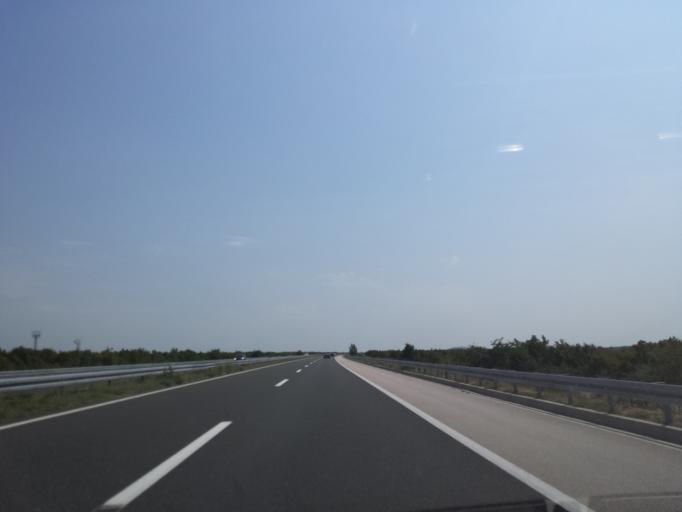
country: HR
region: Zadarska
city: Benkovac
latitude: 43.9893
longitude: 15.6250
